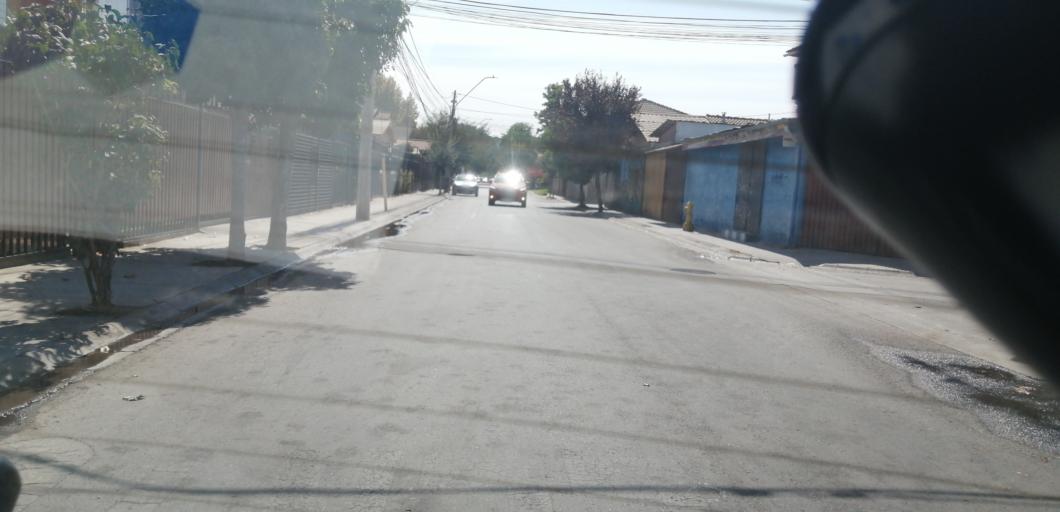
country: CL
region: Santiago Metropolitan
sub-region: Provincia de Santiago
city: Lo Prado
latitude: -33.4549
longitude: -70.7470
